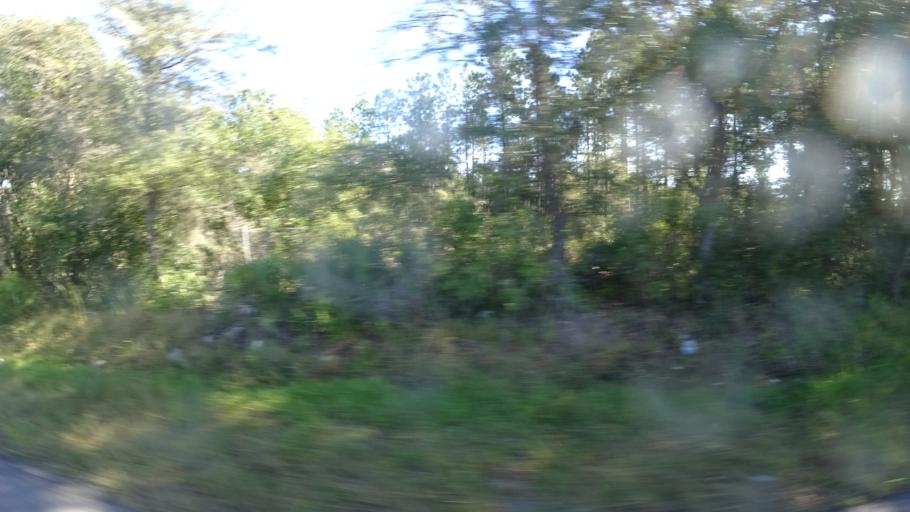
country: US
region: Florida
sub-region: Hillsborough County
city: Sun City Center
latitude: 27.6627
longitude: -82.3588
